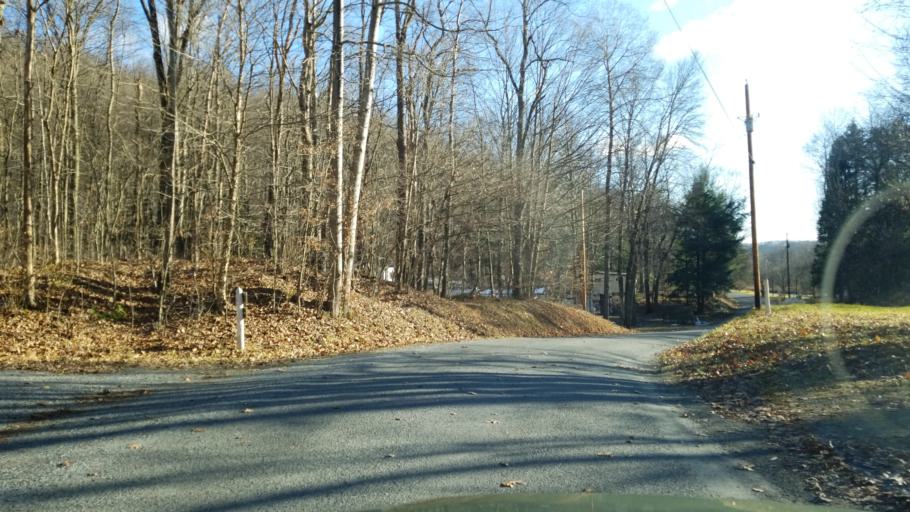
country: US
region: Pennsylvania
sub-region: Jefferson County
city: Brockway
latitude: 41.2663
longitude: -78.8046
